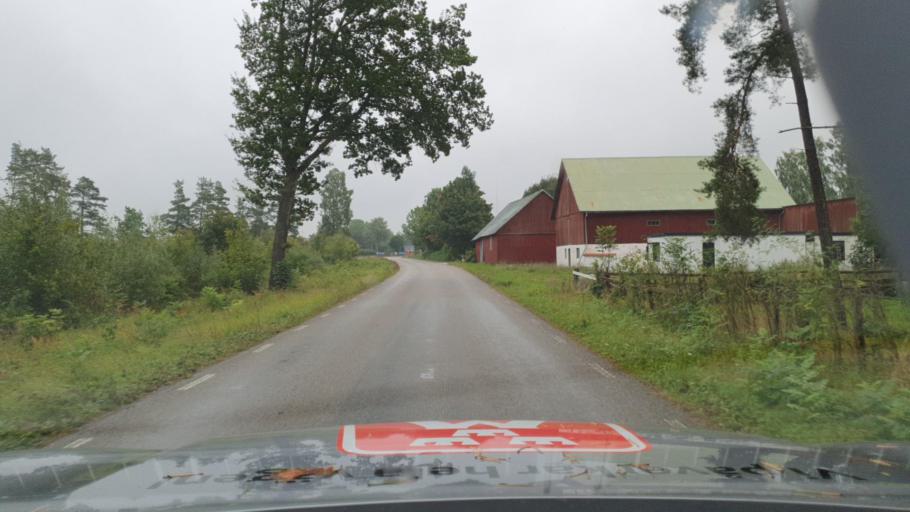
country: SE
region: Gotland
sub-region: Gotland
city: Slite
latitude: 57.7590
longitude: 18.5564
